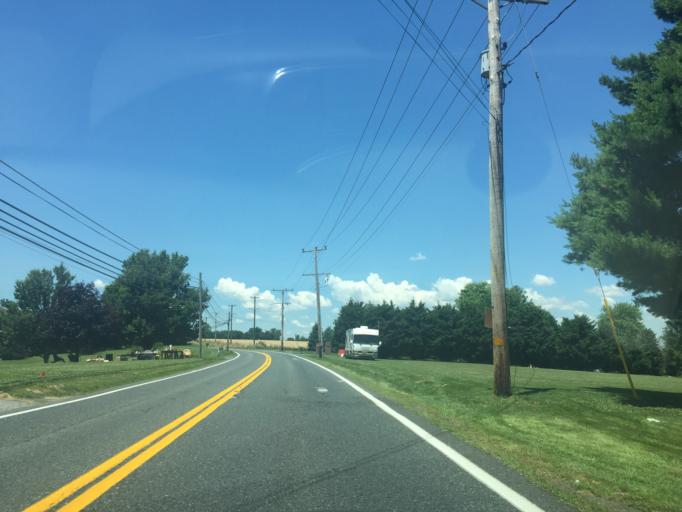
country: US
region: Maryland
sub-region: Harford County
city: Jarrettsville
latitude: 39.6083
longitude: -76.4967
